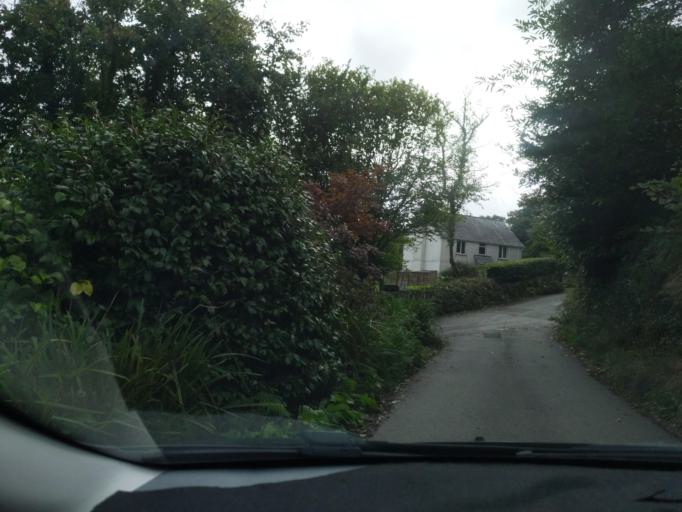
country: GB
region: England
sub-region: Cornwall
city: Lostwithiel
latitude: 50.3995
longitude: -4.7020
